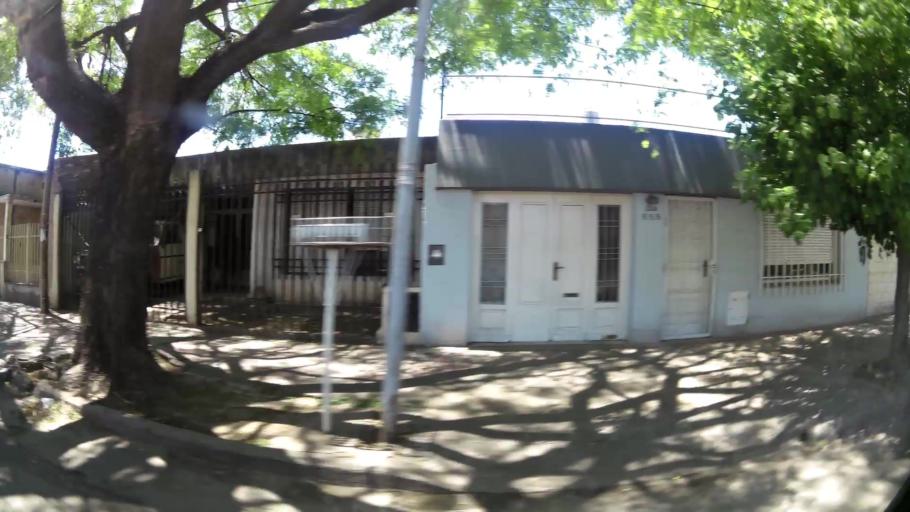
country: AR
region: Cordoba
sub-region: Departamento de Capital
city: Cordoba
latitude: -31.3829
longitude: -64.1372
